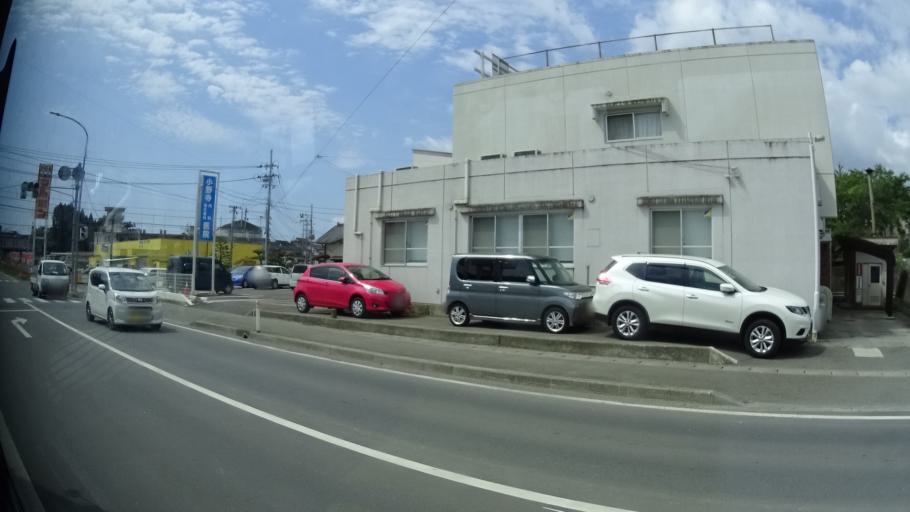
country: JP
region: Iwate
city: Ofunato
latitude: 38.8825
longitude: 141.5747
